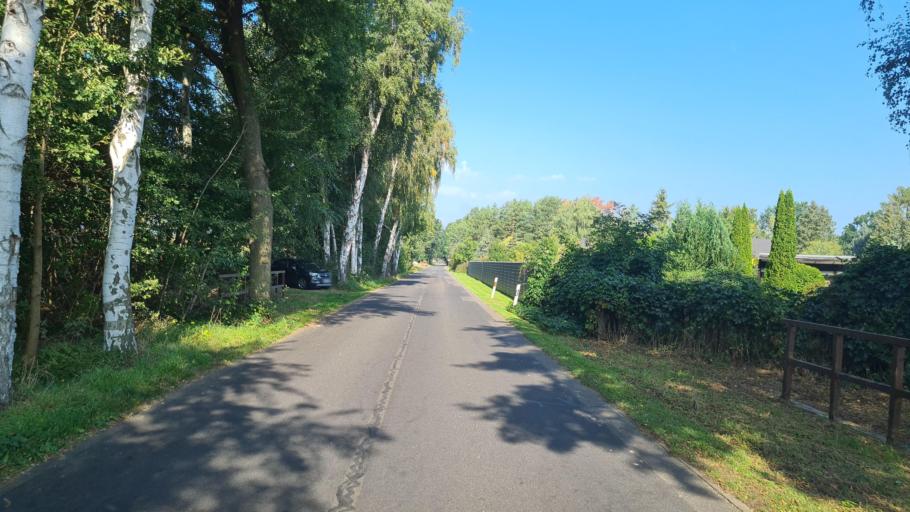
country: DE
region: Brandenburg
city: Kolkwitz
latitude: 51.7406
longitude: 14.2477
